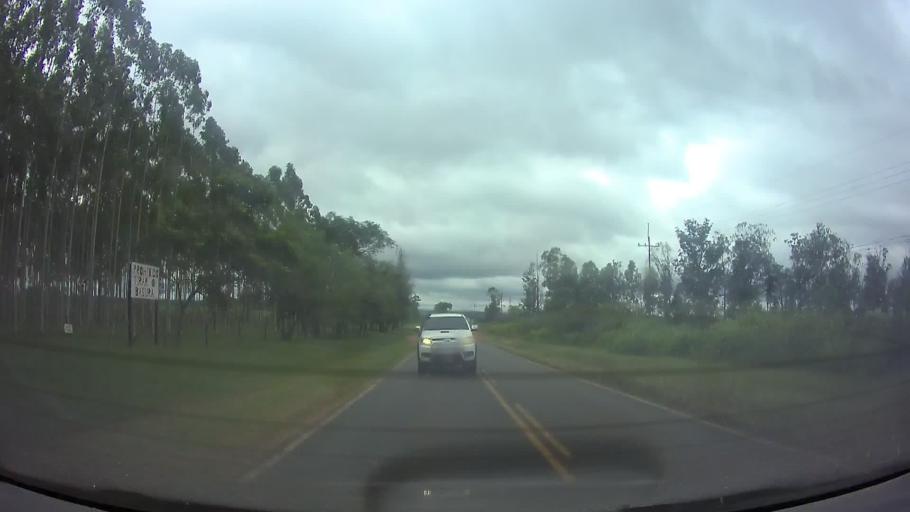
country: PY
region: Central
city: Guarambare
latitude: -25.5098
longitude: -57.4871
